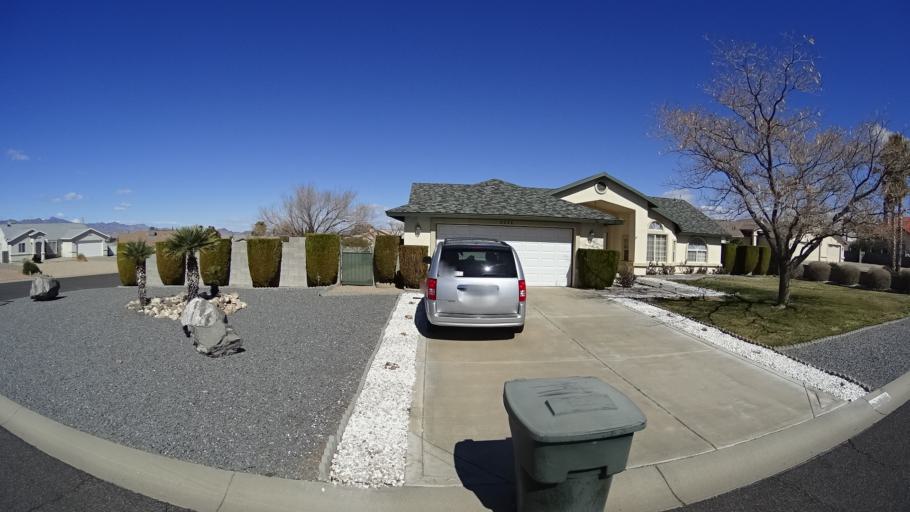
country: US
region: Arizona
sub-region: Mohave County
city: Kingman
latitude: 35.1990
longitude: -113.9678
